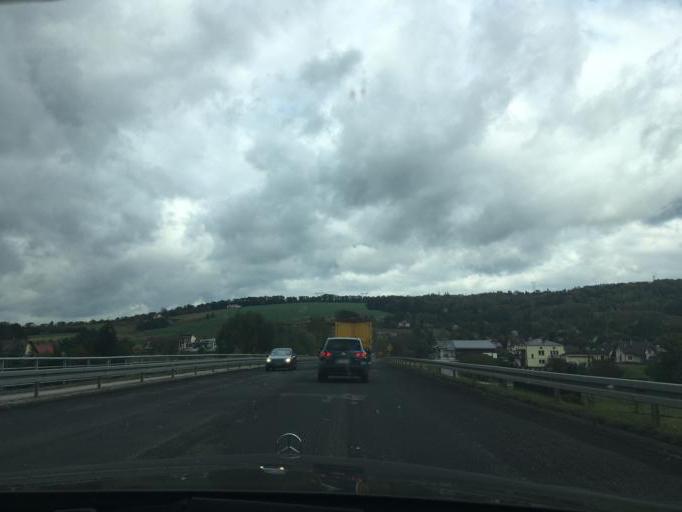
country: PL
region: Subcarpathian Voivodeship
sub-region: Powiat strzyzowski
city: Babica
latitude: 49.9306
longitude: 21.8722
